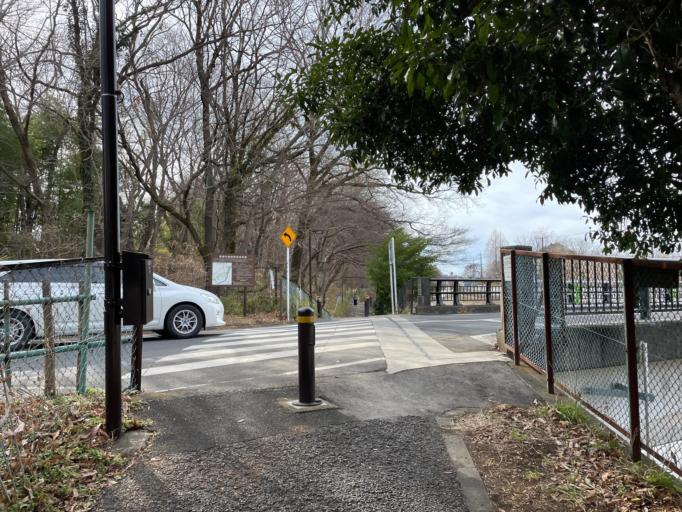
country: JP
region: Saitama
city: Tokorozawa
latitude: 35.7816
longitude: 139.5078
